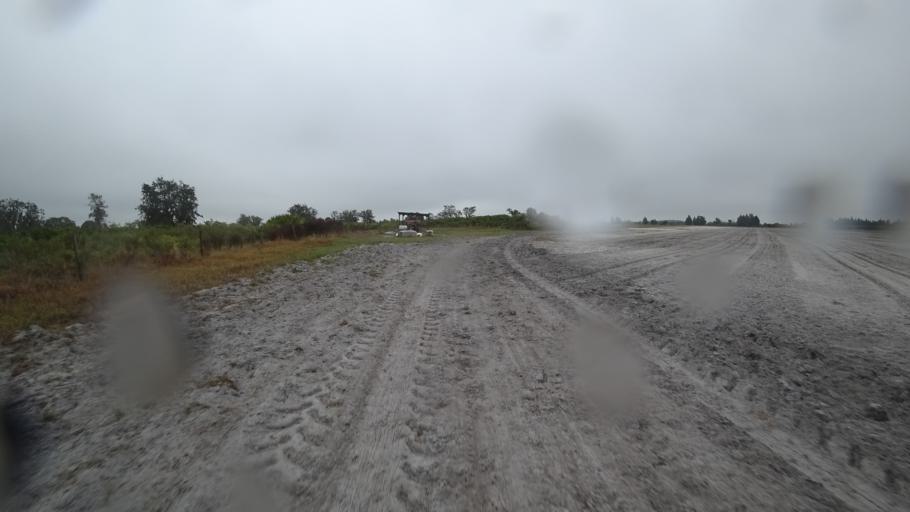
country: US
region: Florida
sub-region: Sarasota County
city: Warm Mineral Springs
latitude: 27.3054
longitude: -82.1582
